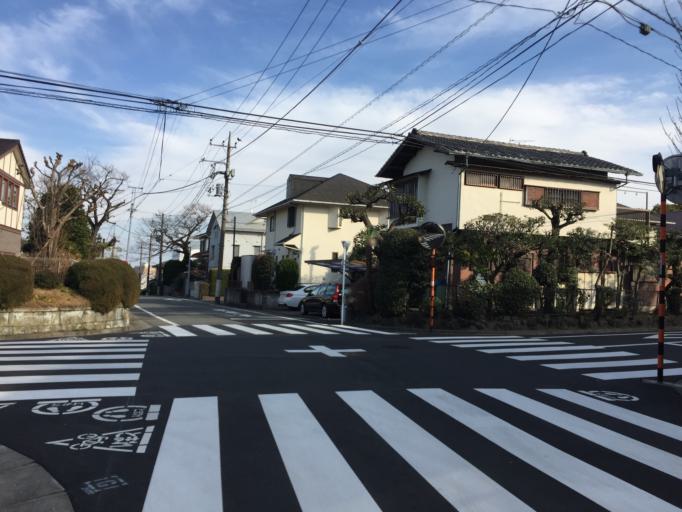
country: JP
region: Kanagawa
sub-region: Kawasaki-shi
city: Kawasaki
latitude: 35.5950
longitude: 139.6660
